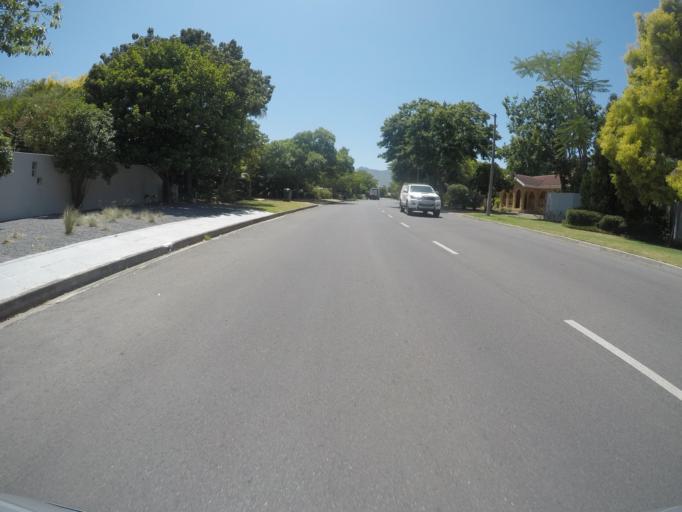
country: ZA
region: Western Cape
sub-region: Cape Winelands District Municipality
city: Stellenbosch
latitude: -33.9453
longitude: 18.8479
